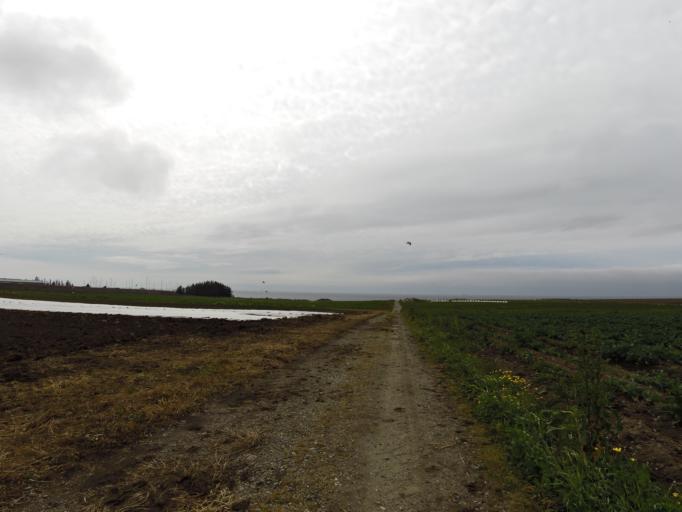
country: NO
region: Rogaland
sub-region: Ha
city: Naerbo
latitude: 58.6342
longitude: 5.5974
